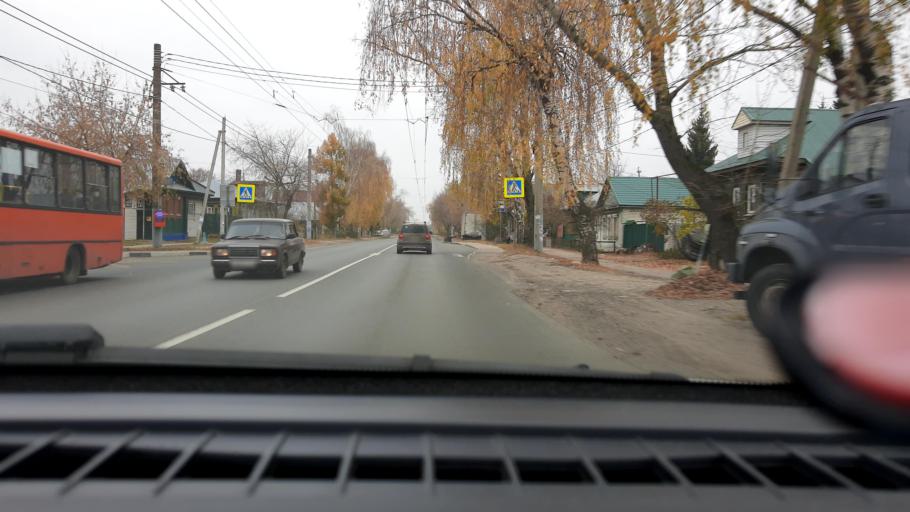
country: RU
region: Nizjnij Novgorod
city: Gorbatovka
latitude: 56.3877
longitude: 43.7700
